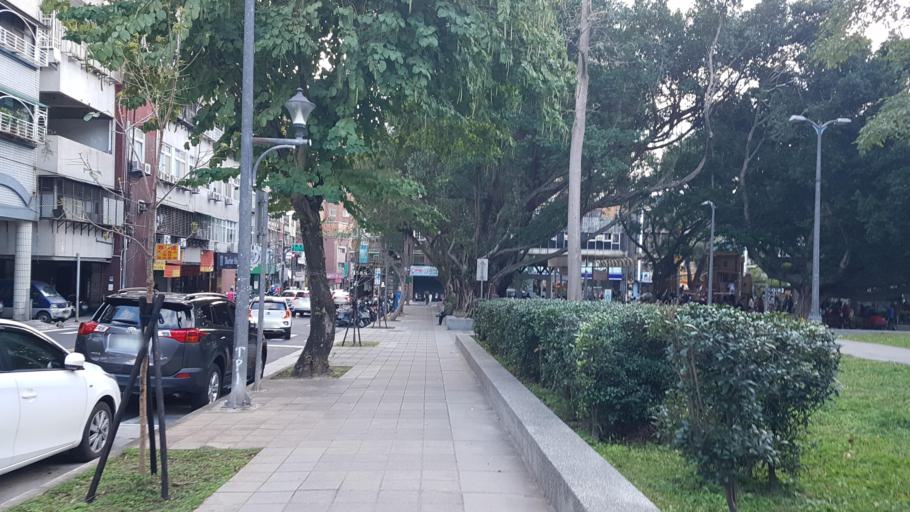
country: TW
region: Taipei
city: Taipei
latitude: 25.1389
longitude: 121.5031
